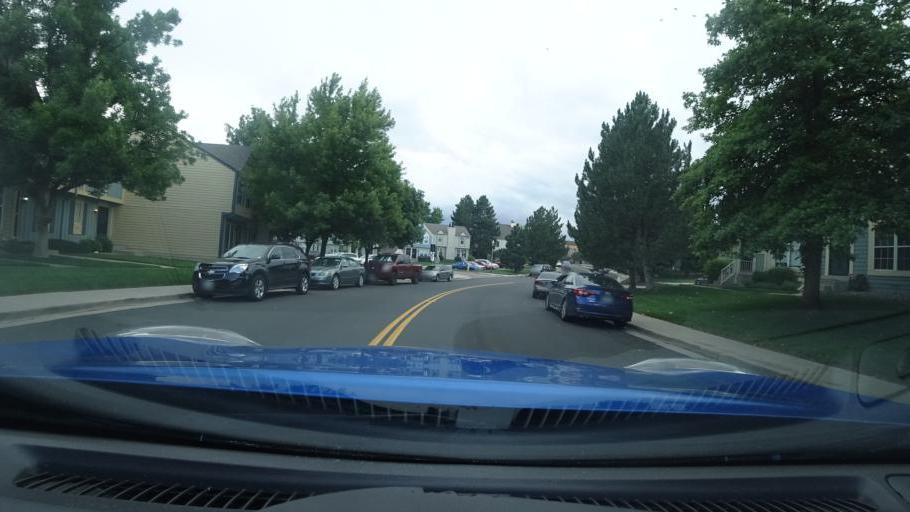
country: US
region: Colorado
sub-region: Adams County
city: Aurora
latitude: 39.6873
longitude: -104.8067
